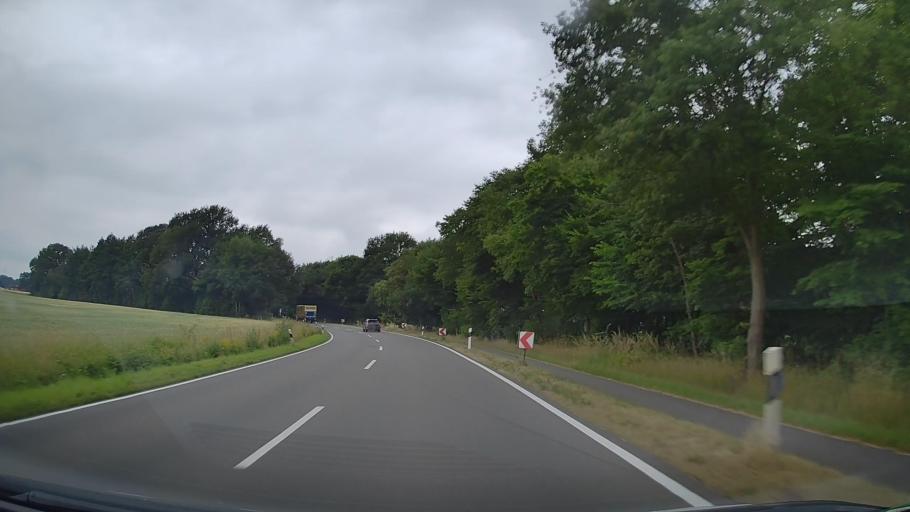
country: DE
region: Lower Saxony
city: Dinklage
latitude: 52.6803
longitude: 8.0859
